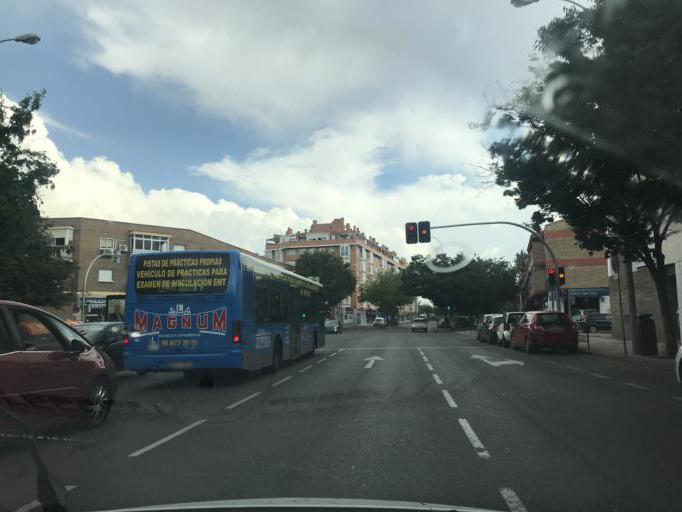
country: ES
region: Madrid
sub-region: Provincia de Madrid
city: Barajas de Madrid
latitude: 40.4719
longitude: -3.5818
